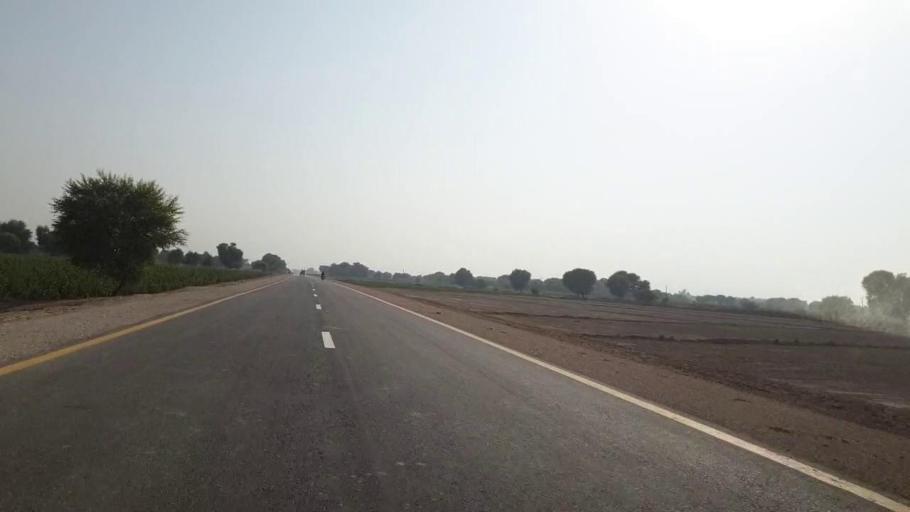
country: PK
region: Sindh
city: Bhan
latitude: 26.5239
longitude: 67.7888
